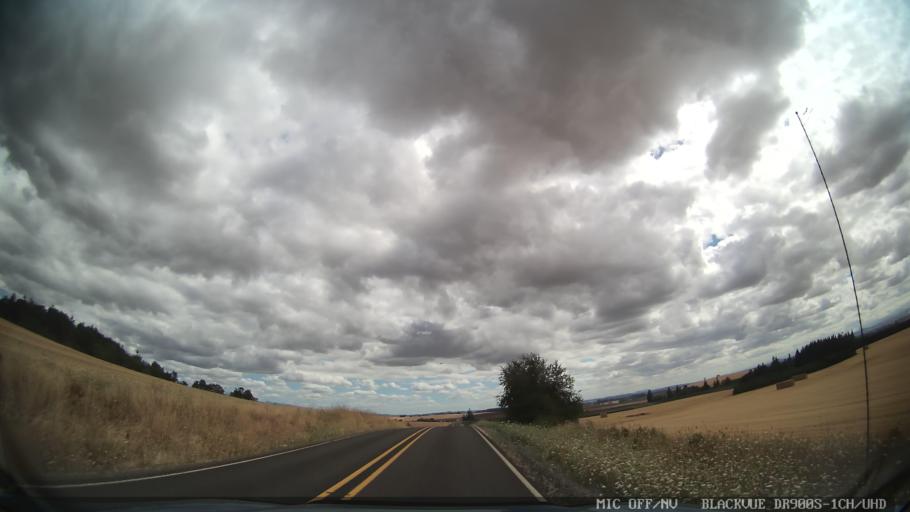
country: US
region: Oregon
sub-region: Marion County
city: Sublimity
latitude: 44.8646
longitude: -122.7386
